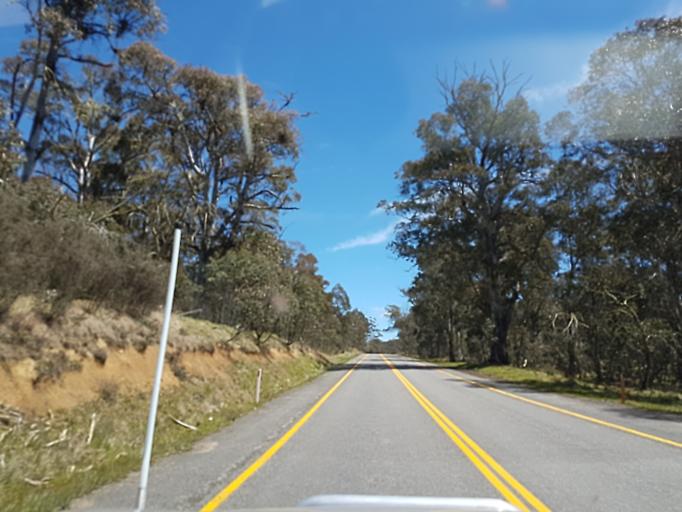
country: AU
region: Victoria
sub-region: Alpine
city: Mount Beauty
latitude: -37.0495
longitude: 147.3205
